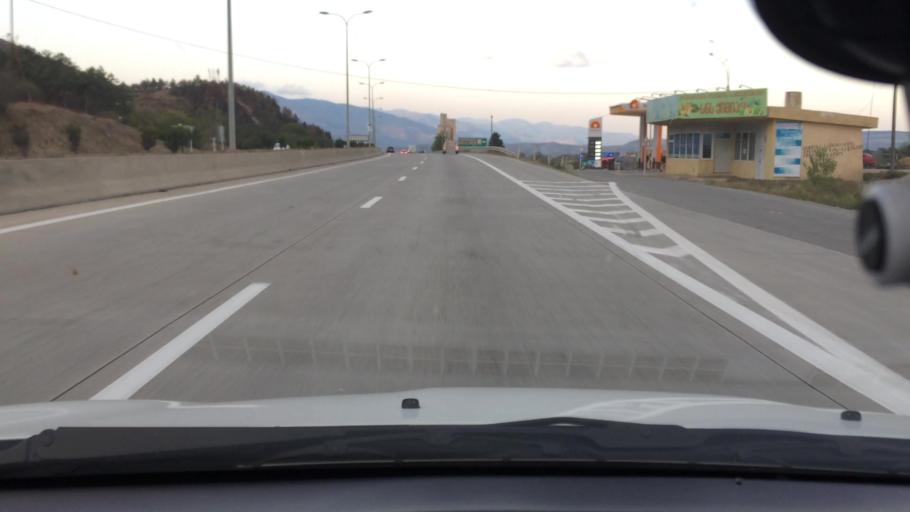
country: GE
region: Shida Kartli
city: Gori
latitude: 42.0191
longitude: 44.1489
